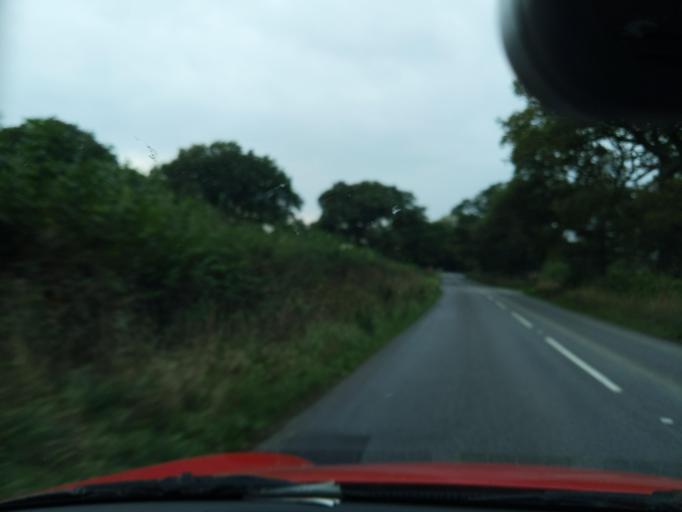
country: GB
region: England
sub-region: Devon
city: Okehampton
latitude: 50.8023
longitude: -4.0561
